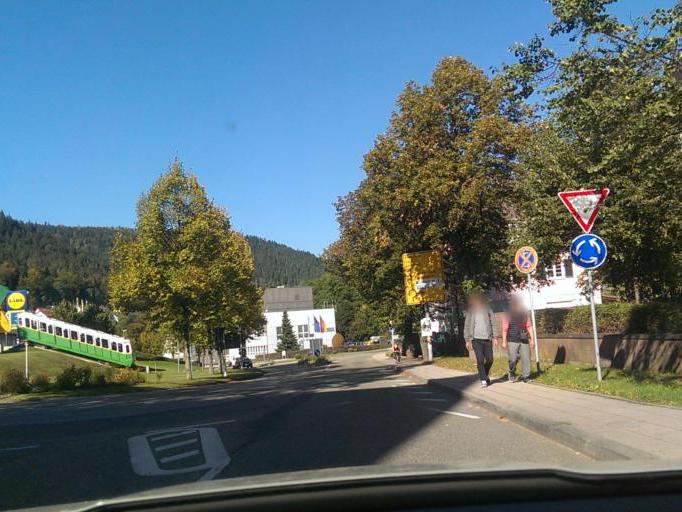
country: DE
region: Baden-Wuerttemberg
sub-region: Karlsruhe Region
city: Bad Wildbad
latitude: 48.7553
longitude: 8.5525
